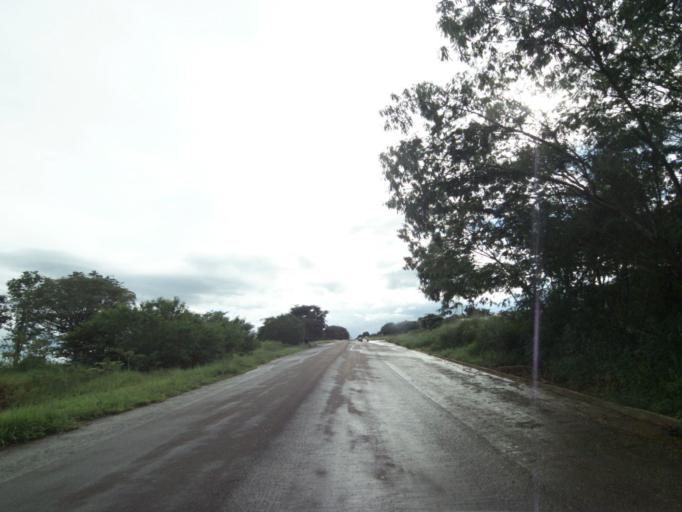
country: BR
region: Goias
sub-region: Itaberai
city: Itaberai
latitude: -15.9179
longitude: -49.5956
